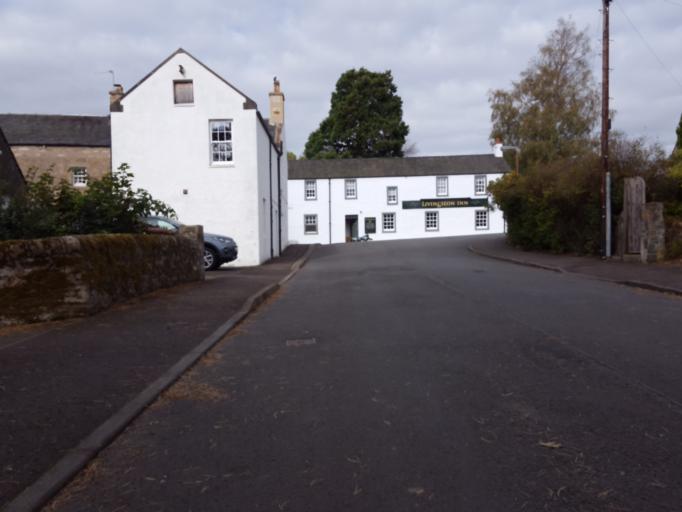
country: GB
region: Scotland
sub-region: West Lothian
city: Livingston
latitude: 55.8851
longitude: -3.5394
